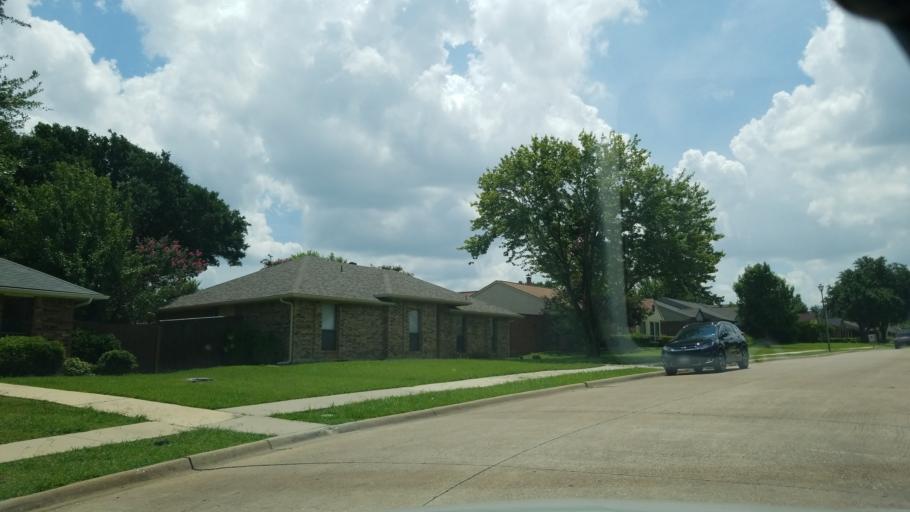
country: US
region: Texas
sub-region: Dallas County
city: Coppell
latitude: 32.9669
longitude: -96.9613
